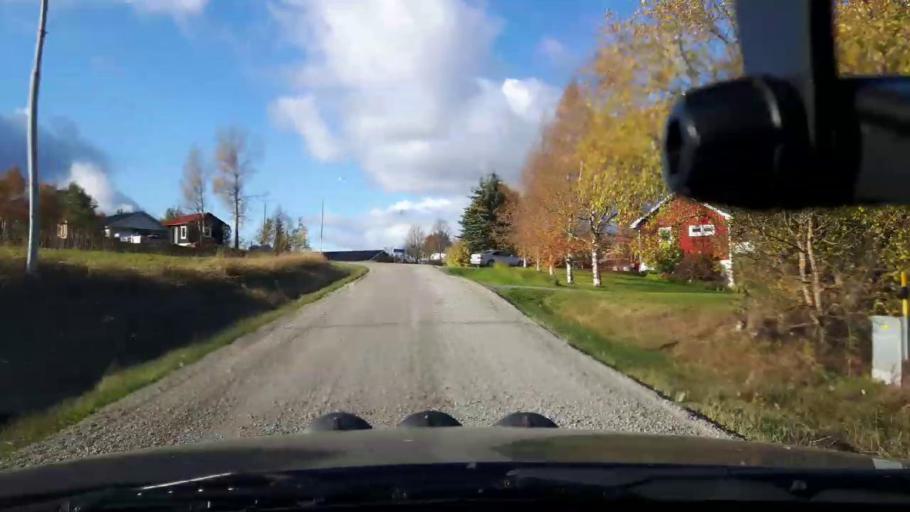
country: SE
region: Jaemtland
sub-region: Bergs Kommun
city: Hoverberg
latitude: 63.0222
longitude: 14.3357
